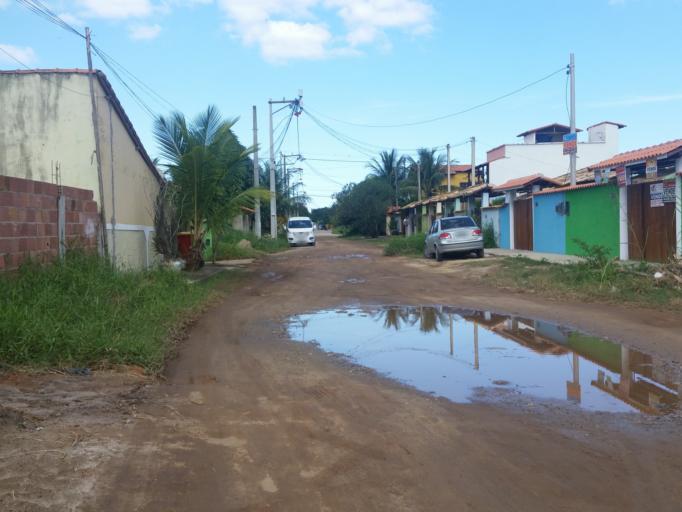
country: BR
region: Rio de Janeiro
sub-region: Marica
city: Marica
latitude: -22.9587
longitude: -42.9667
